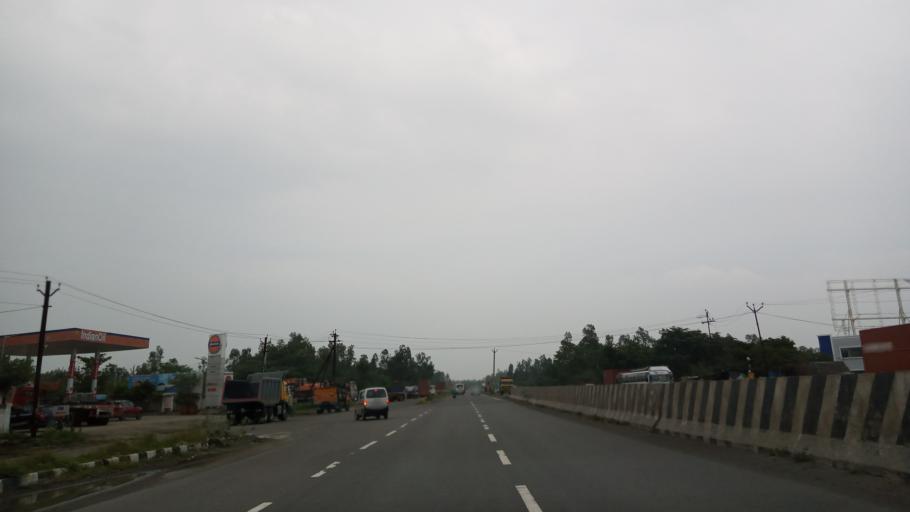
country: IN
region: Tamil Nadu
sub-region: Kancheepuram
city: Madambakkam
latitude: 12.8551
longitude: 79.9503
